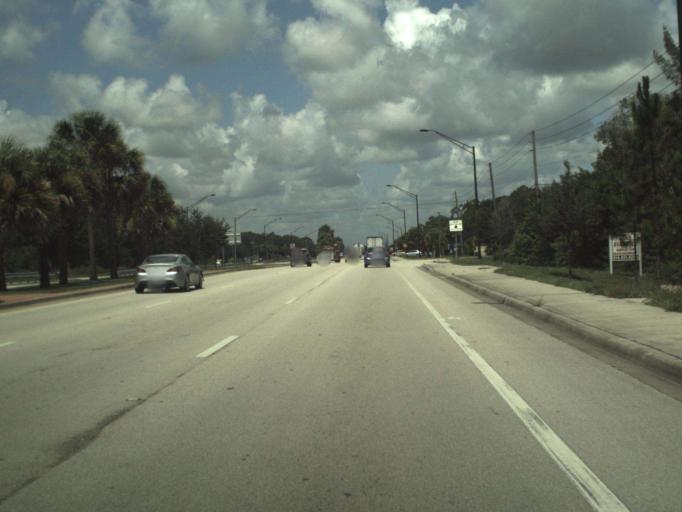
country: US
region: Florida
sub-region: Indian River County
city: West Vero Corridor
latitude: 27.6393
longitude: -80.4985
